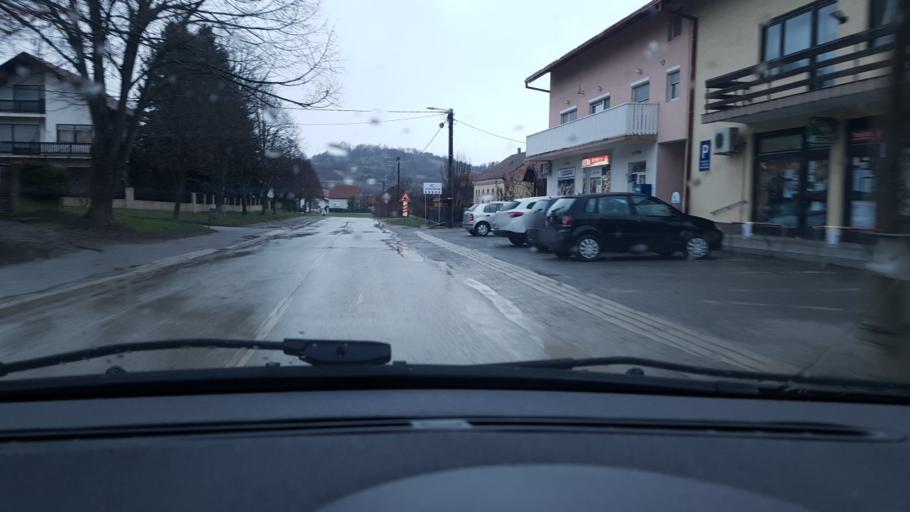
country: HR
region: Krapinsko-Zagorska
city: Oroslavje
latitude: 45.9806
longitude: 15.9730
